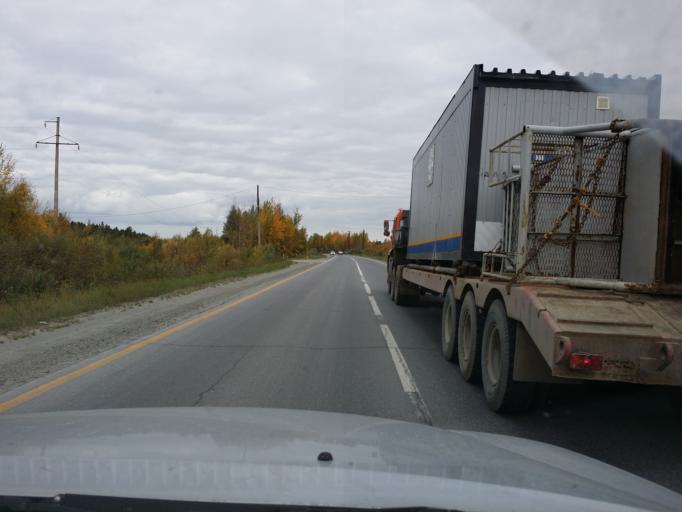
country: RU
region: Khanty-Mansiyskiy Avtonomnyy Okrug
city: Langepas
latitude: 61.1708
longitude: 75.5700
